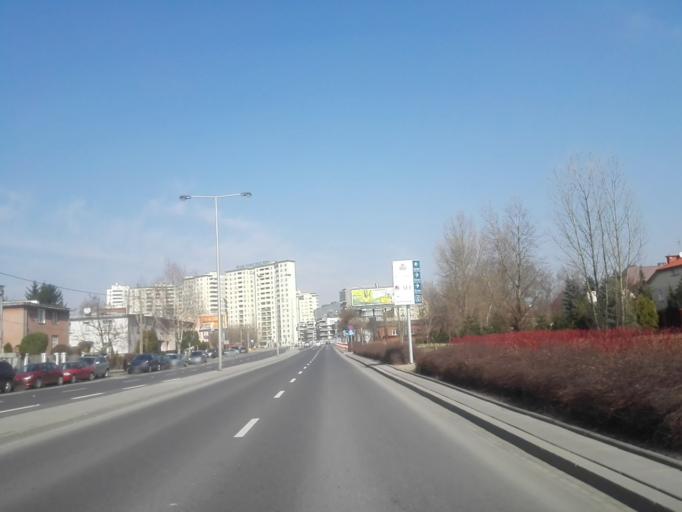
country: PL
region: Masovian Voivodeship
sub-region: Warszawa
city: Mokotow
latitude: 52.1766
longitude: 21.0271
